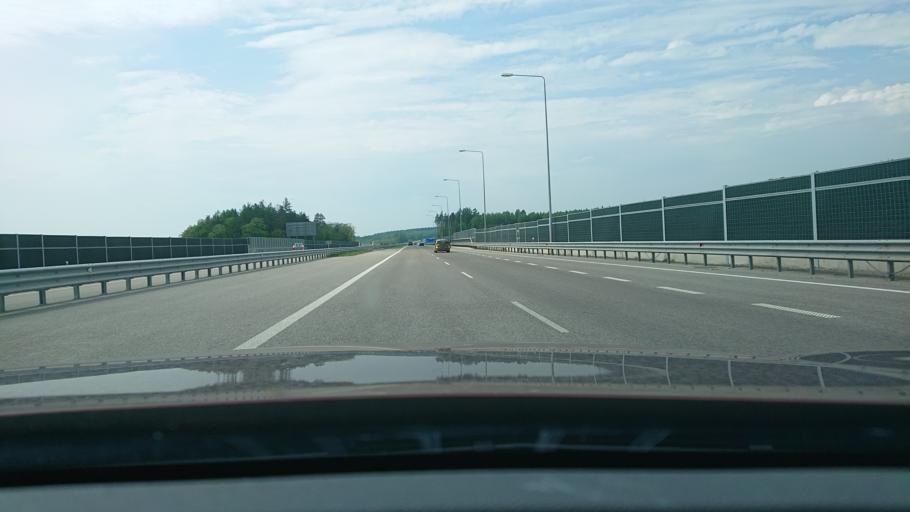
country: PL
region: Subcarpathian Voivodeship
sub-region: Powiat jaroslawski
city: Pawlosiow
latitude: 49.9767
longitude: 22.6359
